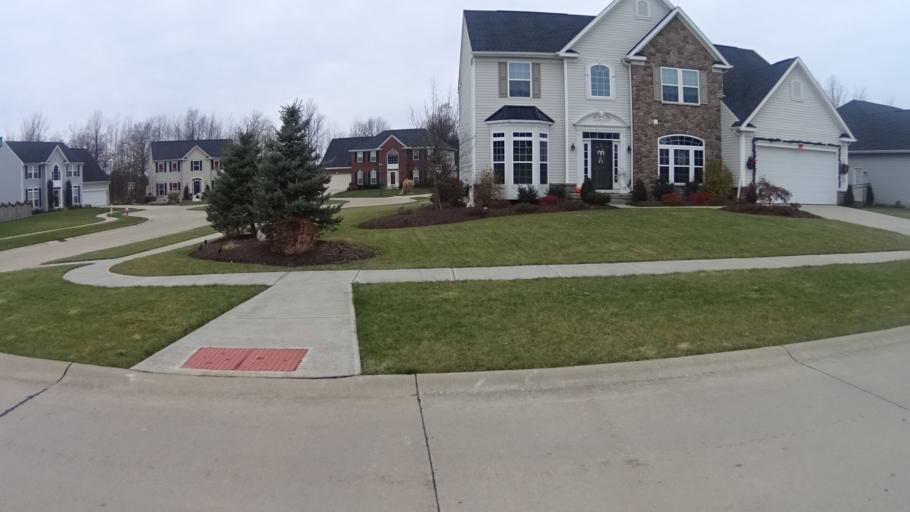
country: US
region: Ohio
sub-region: Lorain County
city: North Ridgeville
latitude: 41.3683
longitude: -81.9754
